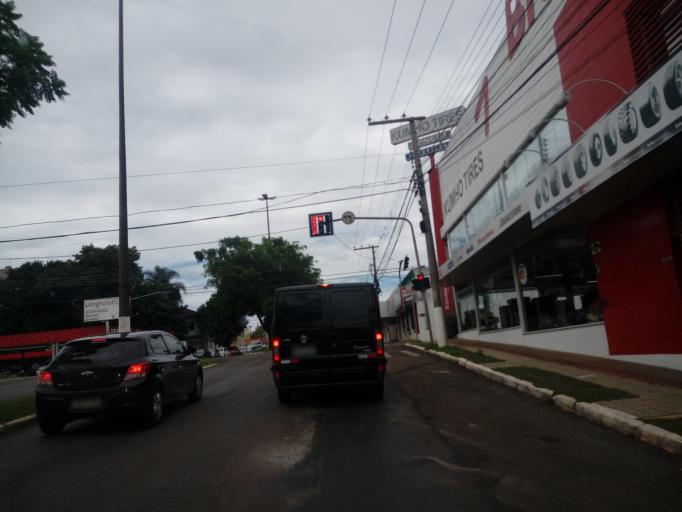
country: BR
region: Santa Catarina
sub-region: Chapeco
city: Chapeco
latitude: -27.0961
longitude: -52.6219
